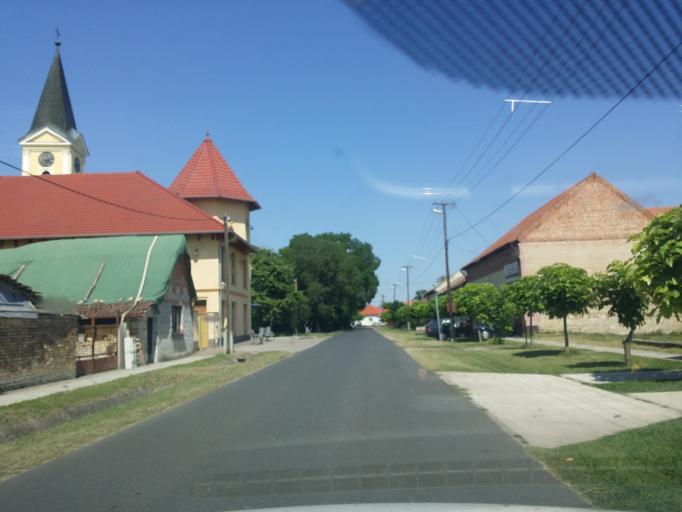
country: HU
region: Bacs-Kiskun
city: Jaszszentlaszlo
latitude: 46.5673
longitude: 19.7621
